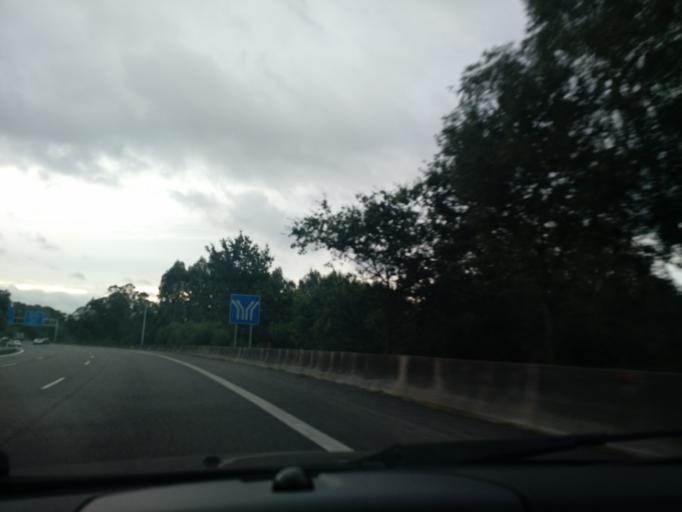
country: ES
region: Galicia
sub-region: Provincia da Coruna
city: Oleiros
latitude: 43.2882
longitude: -8.2918
